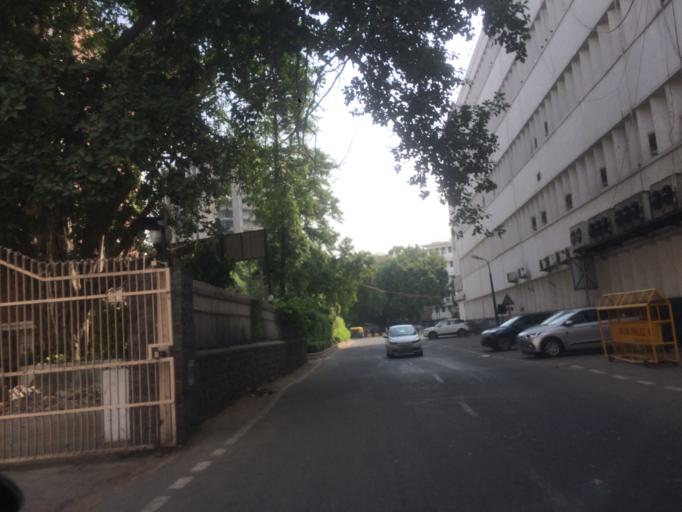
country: IN
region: NCT
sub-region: New Delhi
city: New Delhi
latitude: 28.6232
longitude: 77.2113
